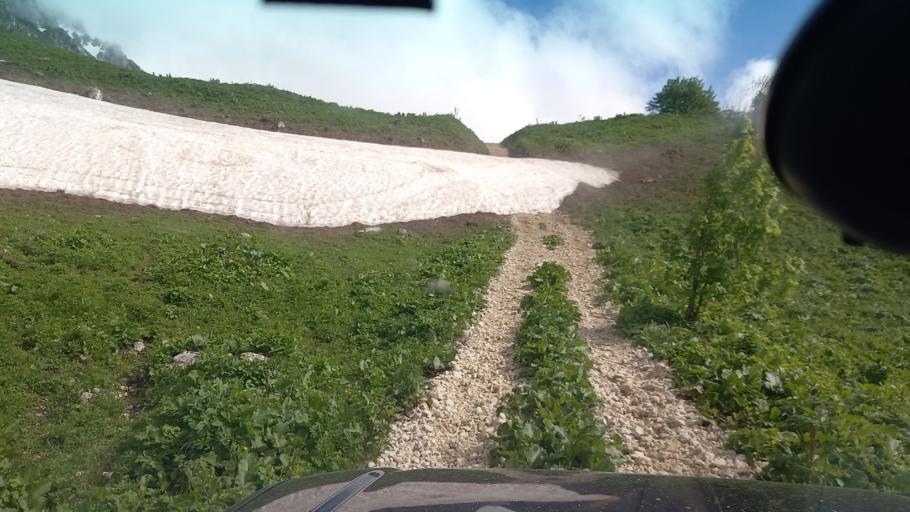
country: RU
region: Krasnodarskiy
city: Neftegorsk
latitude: 44.0105
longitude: 39.8612
